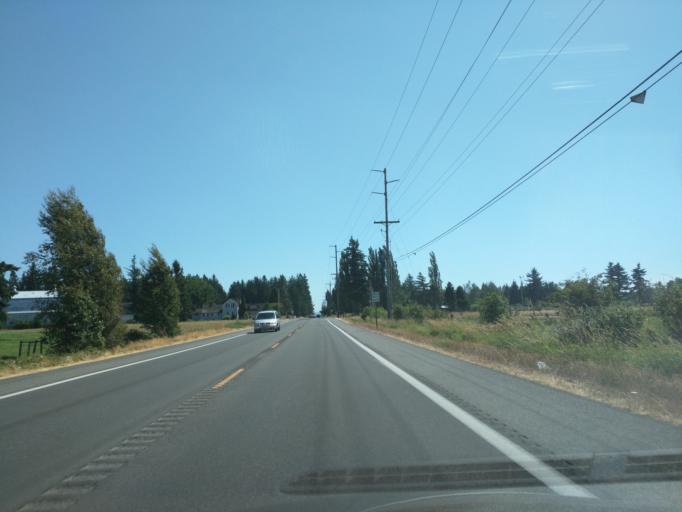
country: US
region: Washington
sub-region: Whatcom County
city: Lynden
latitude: 48.8999
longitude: -122.4424
